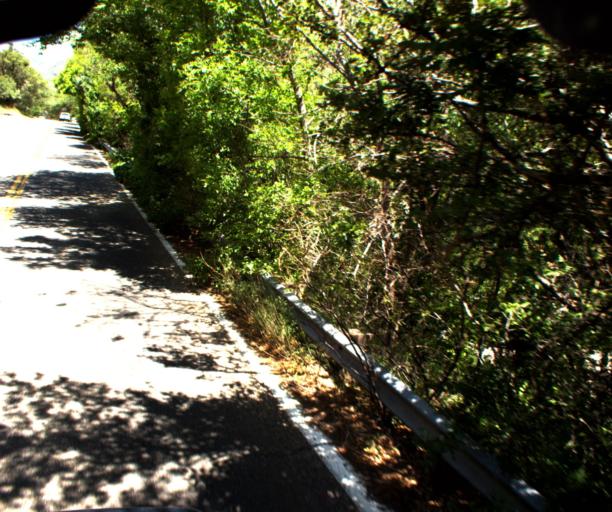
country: US
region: Arizona
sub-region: Coconino County
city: Sedona
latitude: 34.9173
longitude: -111.7305
